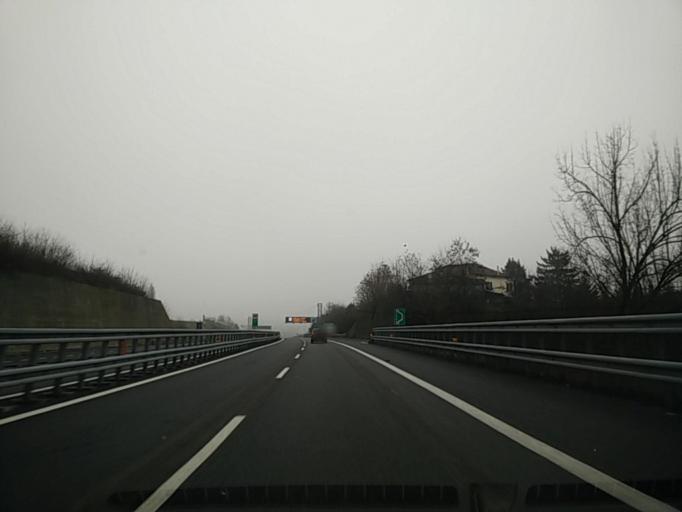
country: IT
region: Piedmont
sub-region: Provincia di Asti
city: Asti
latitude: 44.9153
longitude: 8.2129
